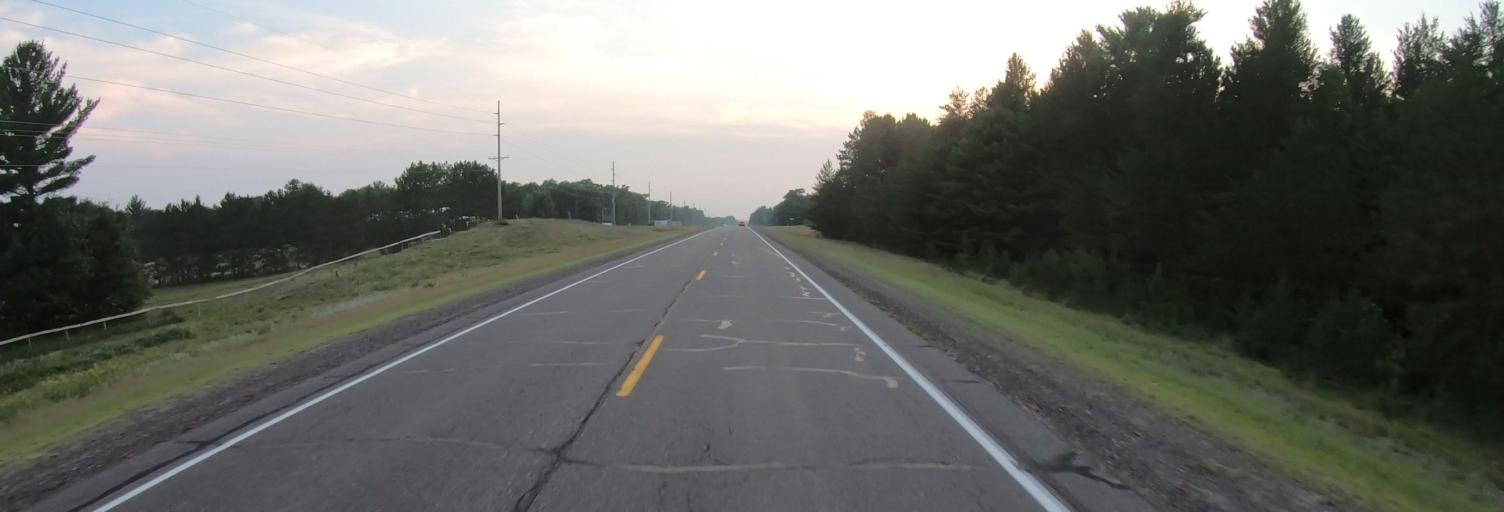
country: US
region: Wisconsin
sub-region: Burnett County
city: Grantsburg
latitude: 45.7731
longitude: -92.7410
